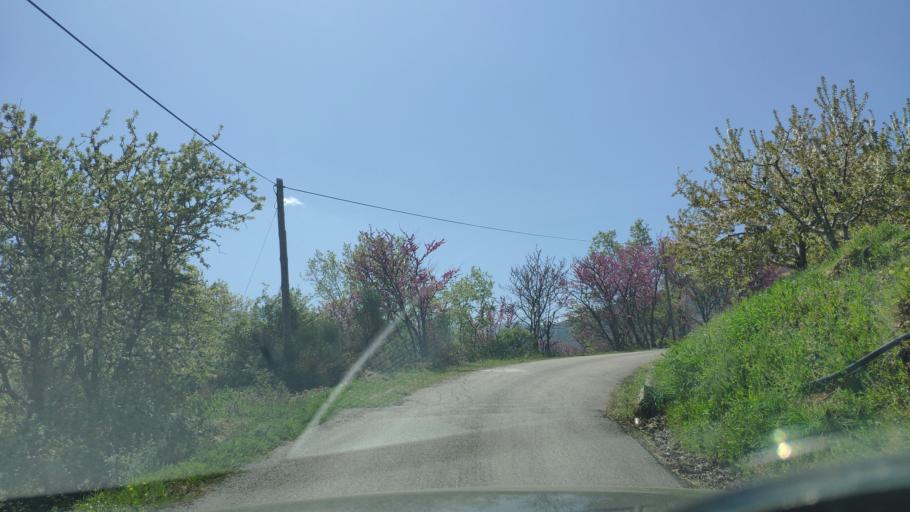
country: GR
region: West Greece
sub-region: Nomos Achaias
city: Akrata
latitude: 38.0842
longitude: 22.3236
